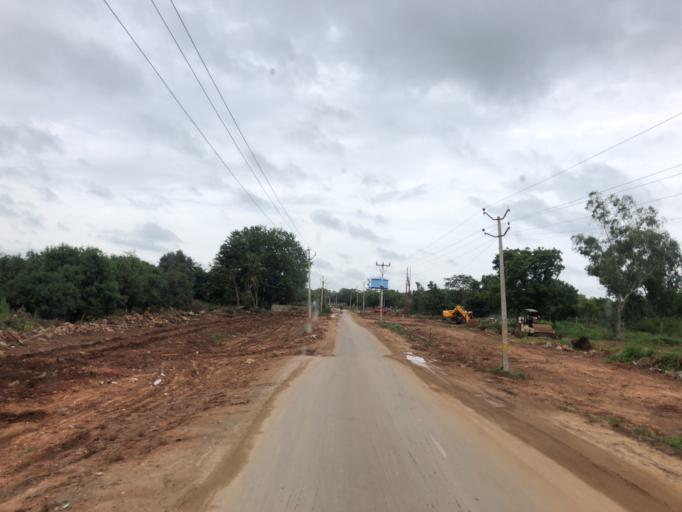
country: IN
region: Telangana
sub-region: Medak
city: Serilingampalle
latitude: 17.4305
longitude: 78.2980
